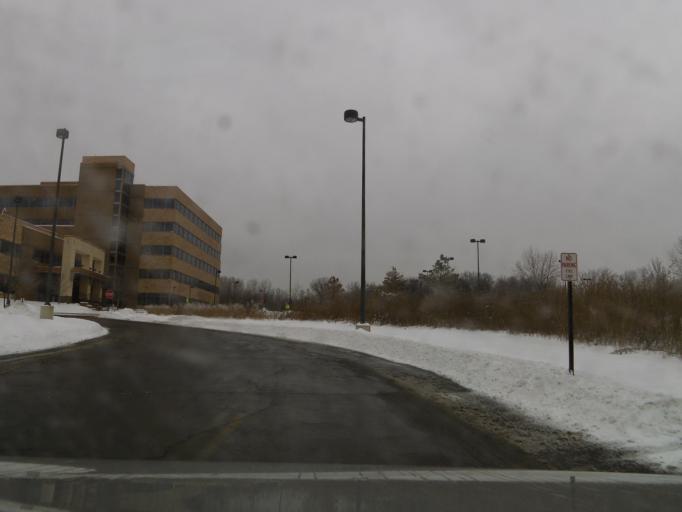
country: US
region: Minnesota
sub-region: Dakota County
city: West Saint Paul
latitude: 44.8838
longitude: -93.0856
